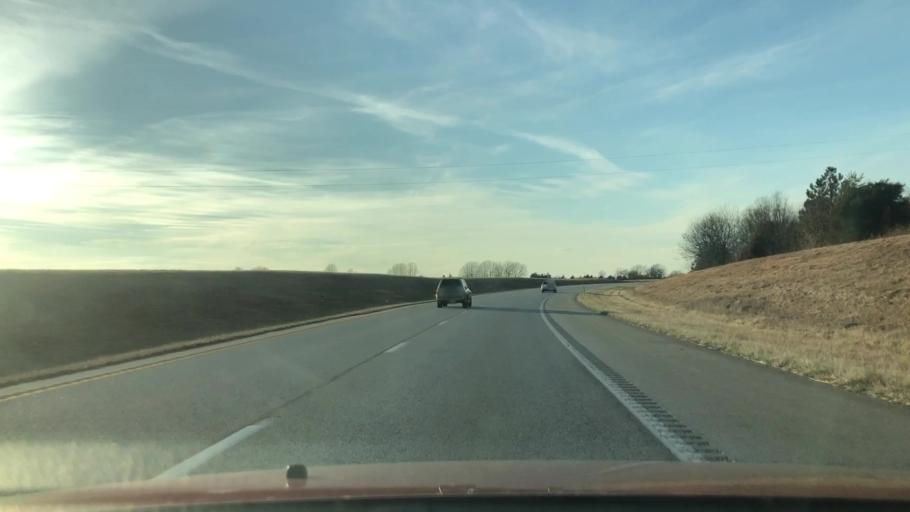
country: US
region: Missouri
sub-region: Webster County
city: Seymour
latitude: 37.1188
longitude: -92.6903
